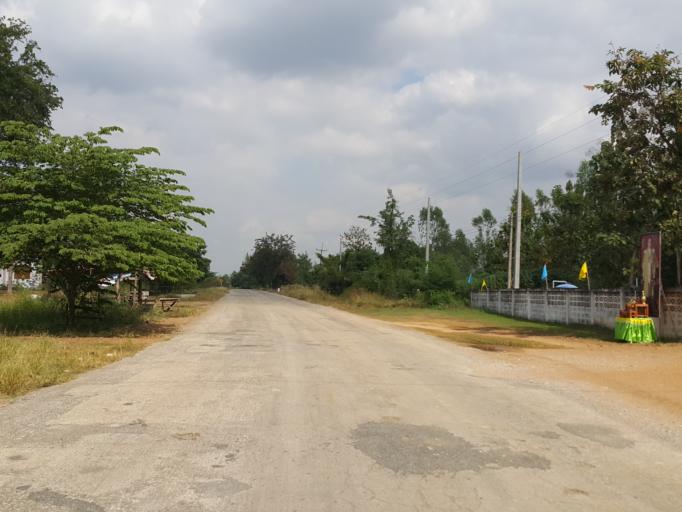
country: TH
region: Sukhothai
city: Thung Saliam
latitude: 17.4089
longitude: 99.5763
